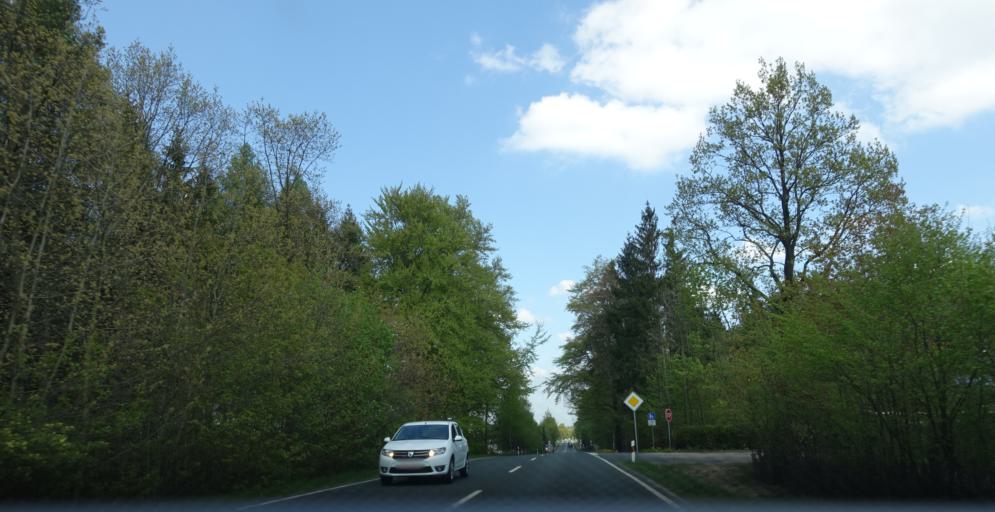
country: DE
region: Saxony
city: Brand-Erbisdorf
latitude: 50.8401
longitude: 13.3220
